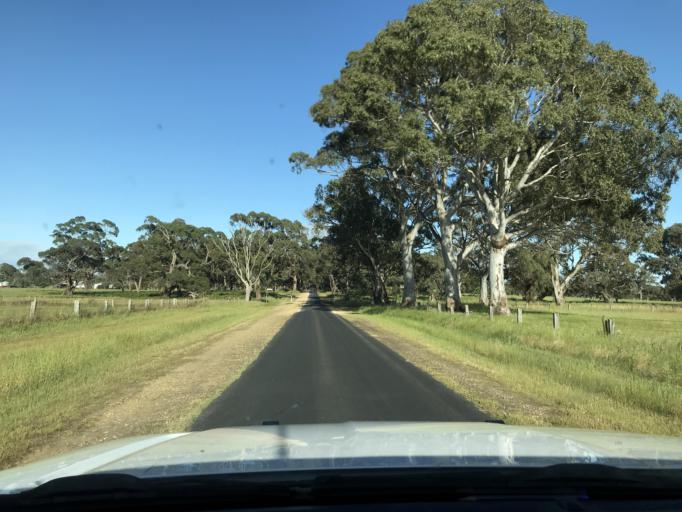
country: AU
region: South Australia
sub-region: Wattle Range
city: Penola
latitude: -37.2027
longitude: 141.0035
